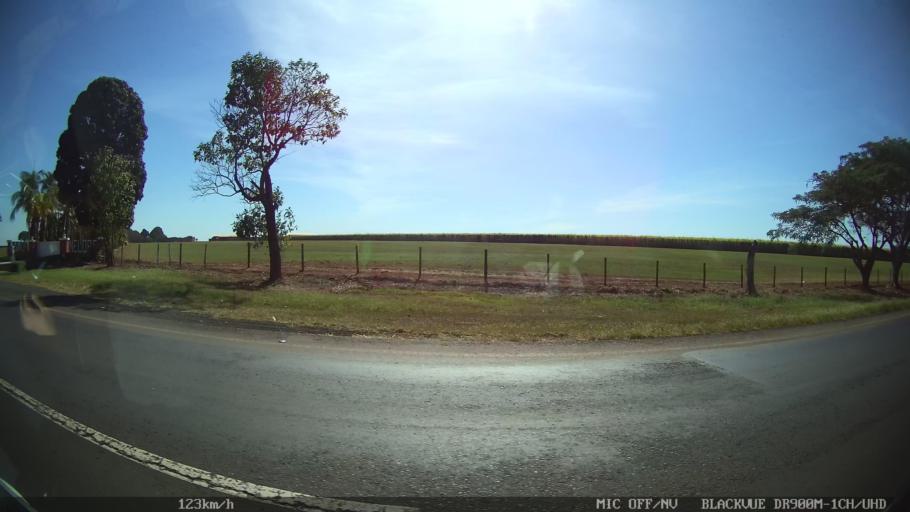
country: BR
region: Sao Paulo
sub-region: Barretos
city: Barretos
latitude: -20.5668
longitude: -48.6639
